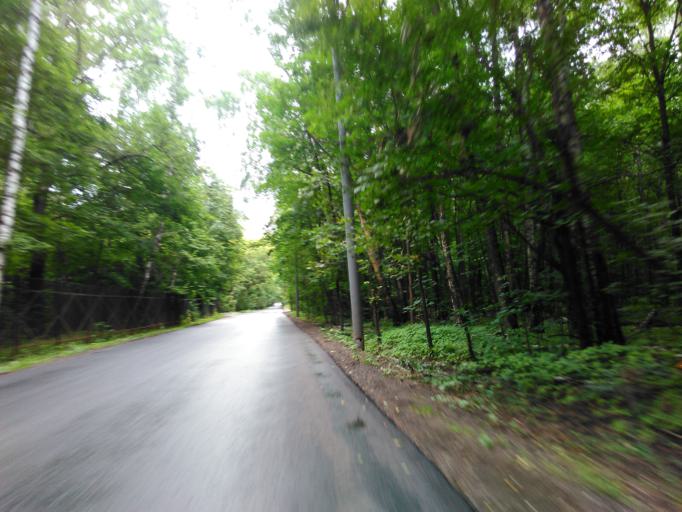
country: RU
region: Moscow
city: Rostokino
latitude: 55.8305
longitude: 37.6820
